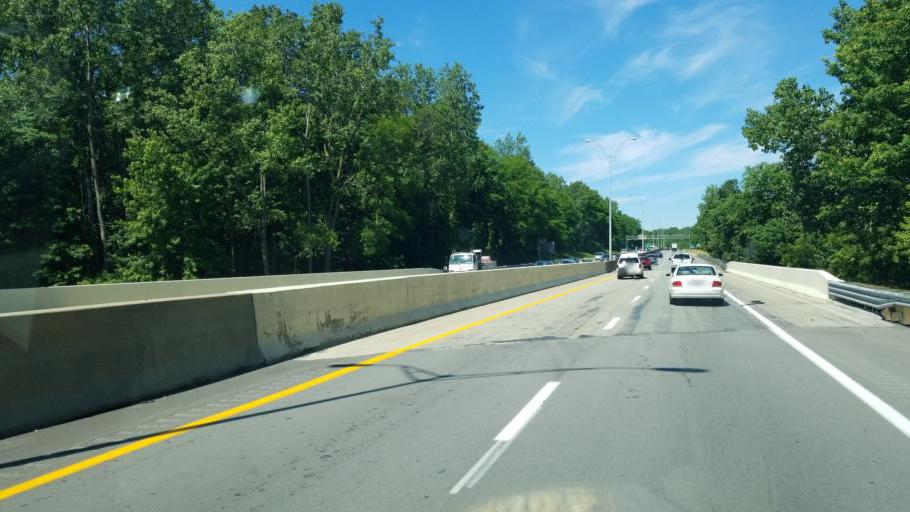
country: US
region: Ohio
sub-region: Lucas County
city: Ottawa Hills
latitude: 41.6898
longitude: -83.6718
